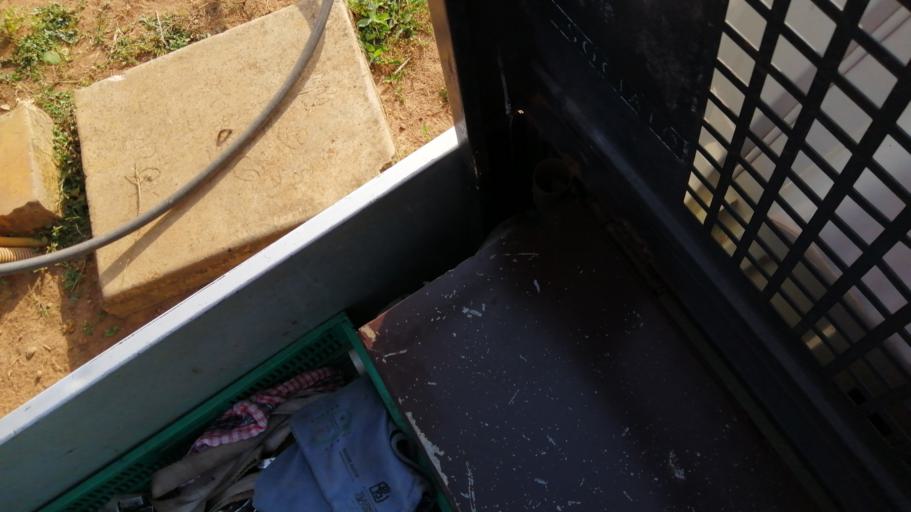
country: GW
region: Oio
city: Mansoa
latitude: 12.0059
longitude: -15.4753
